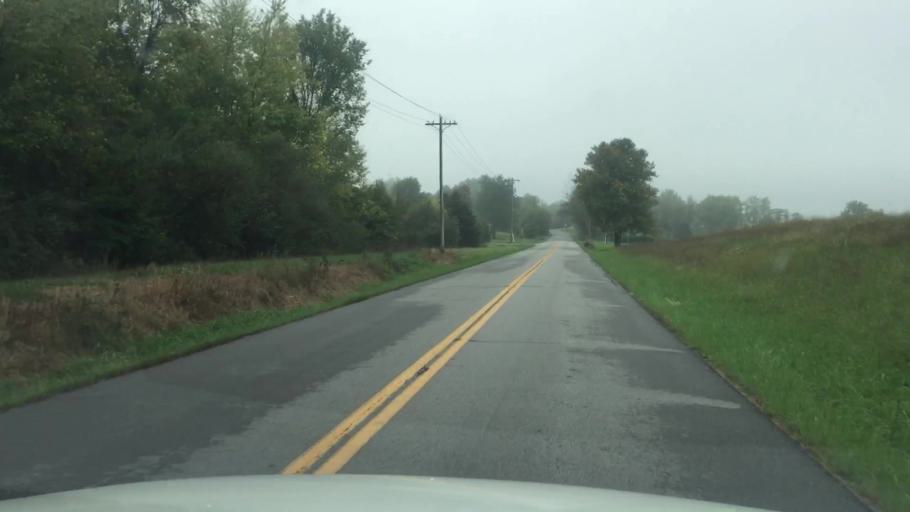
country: US
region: Missouri
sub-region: Boone County
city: Ashland
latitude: 38.8509
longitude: -92.3060
